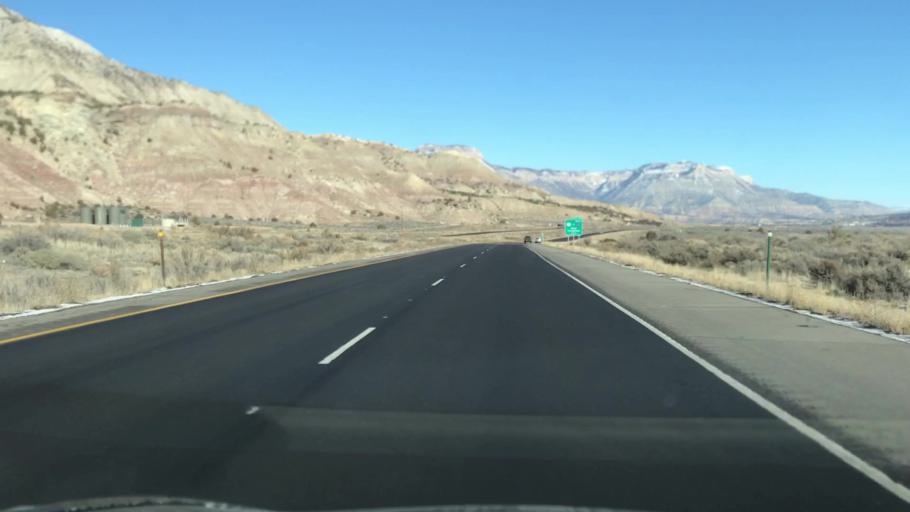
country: US
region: Colorado
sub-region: Garfield County
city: Parachute
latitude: 39.4147
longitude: -108.0927
